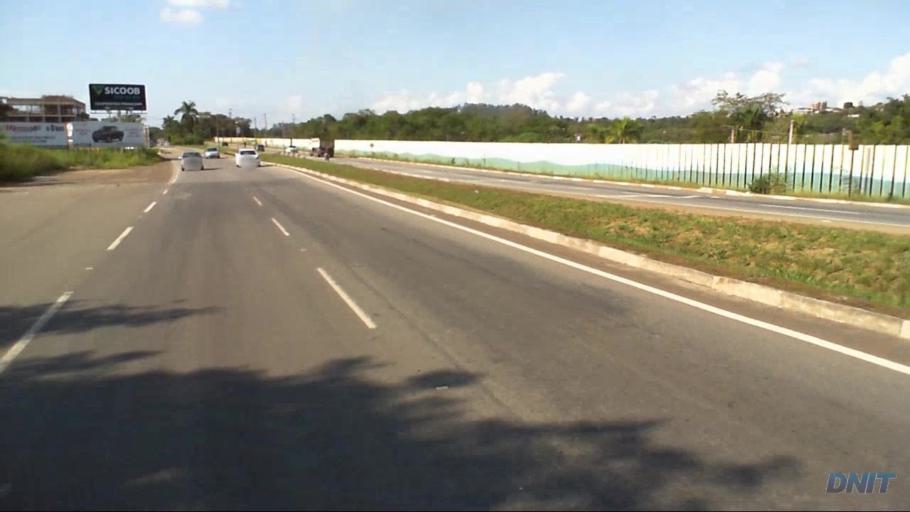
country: BR
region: Minas Gerais
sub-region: Coronel Fabriciano
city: Coronel Fabriciano
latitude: -19.5110
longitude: -42.5746
